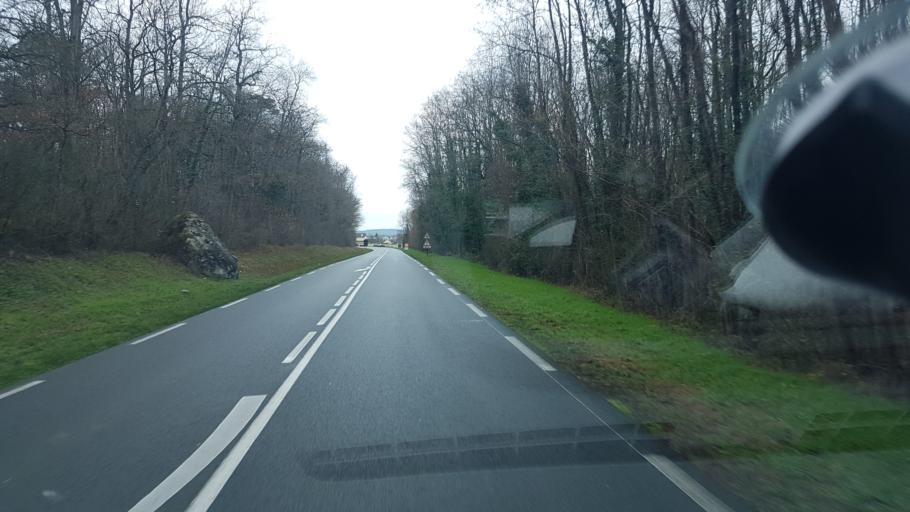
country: FR
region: Ile-de-France
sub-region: Departement de Seine-et-Marne
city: Montcourt-Fromonville
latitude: 48.2755
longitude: 2.7507
